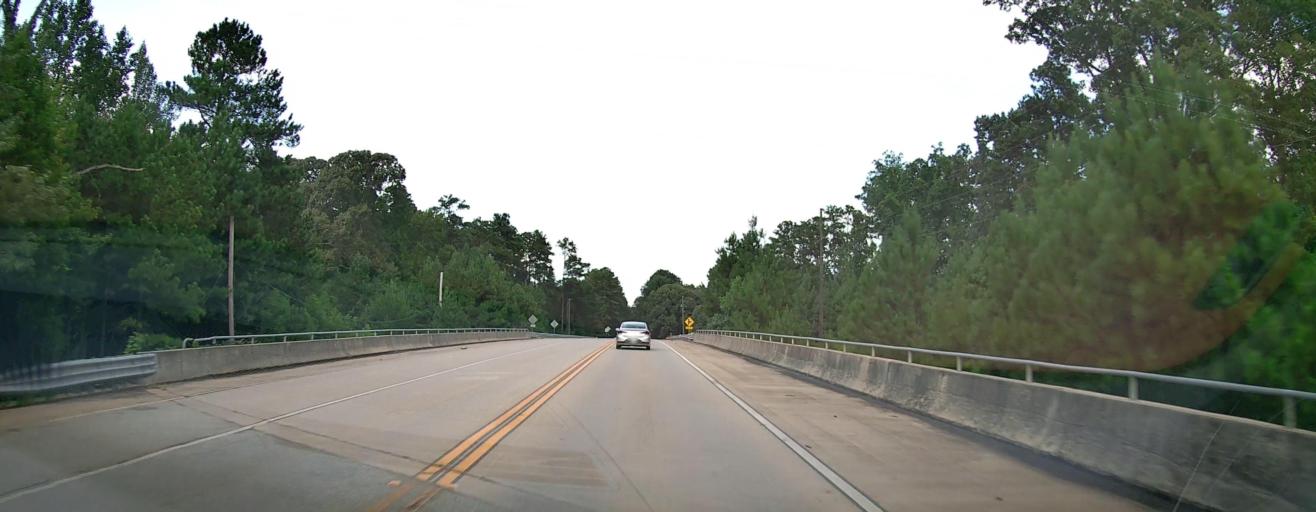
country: US
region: Georgia
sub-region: Coweta County
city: Senoia
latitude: 33.2520
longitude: -84.5596
